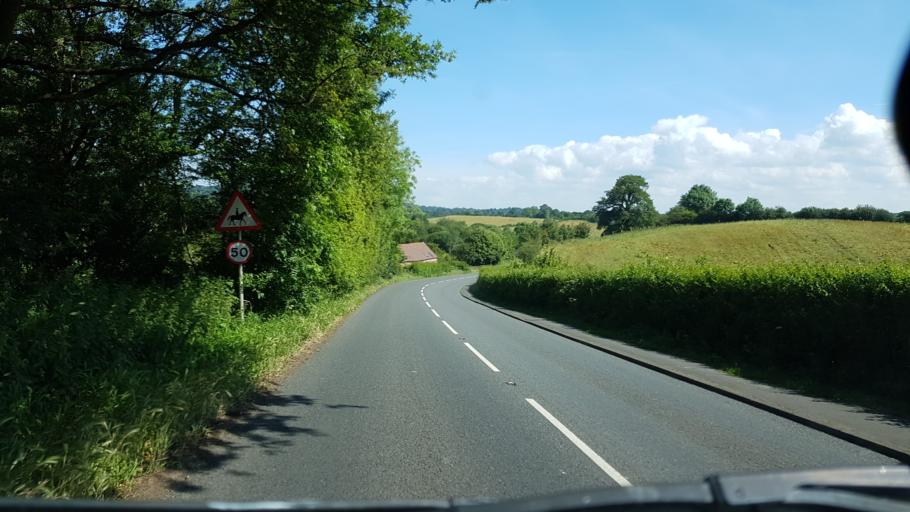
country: GB
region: England
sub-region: Worcestershire
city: Bewdley
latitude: 52.3629
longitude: -2.3021
